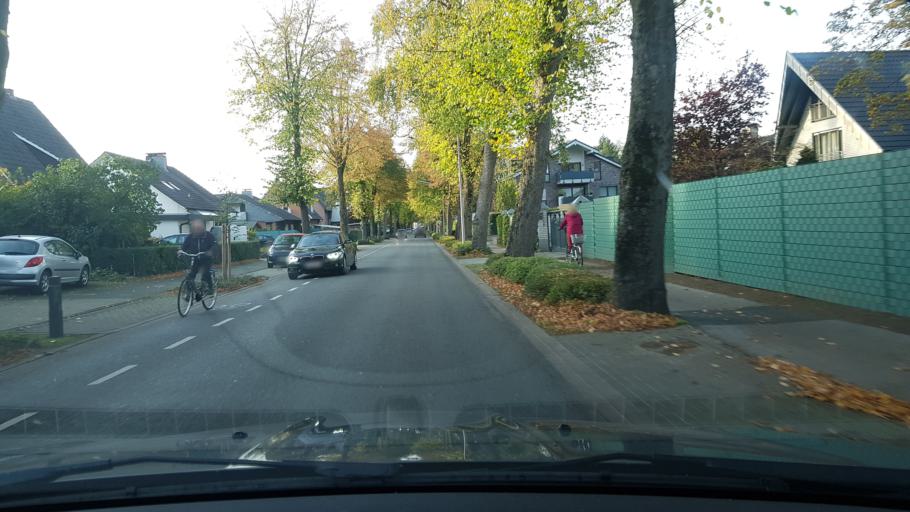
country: DE
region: North Rhine-Westphalia
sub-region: Regierungsbezirk Munster
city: Rhede
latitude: 51.8372
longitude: 6.7041
